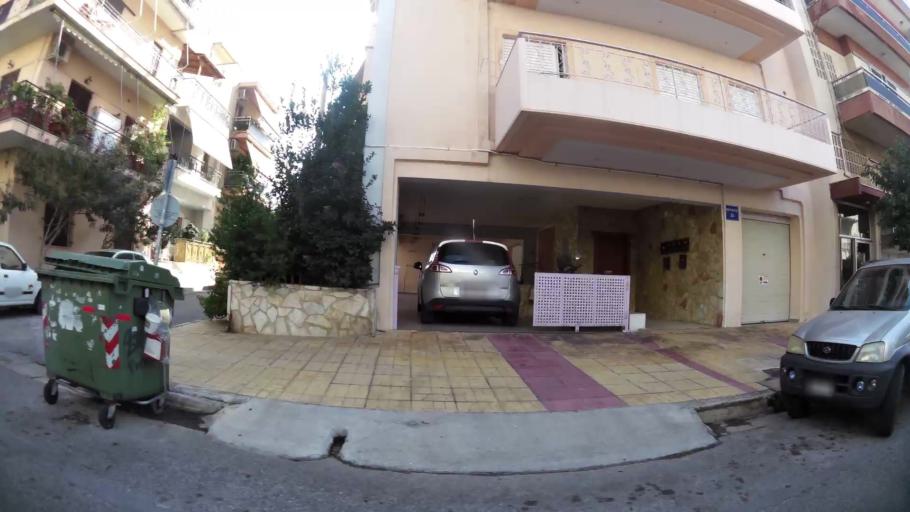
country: GR
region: Attica
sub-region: Nomos Piraios
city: Keratsini
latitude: 37.9637
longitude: 23.6251
